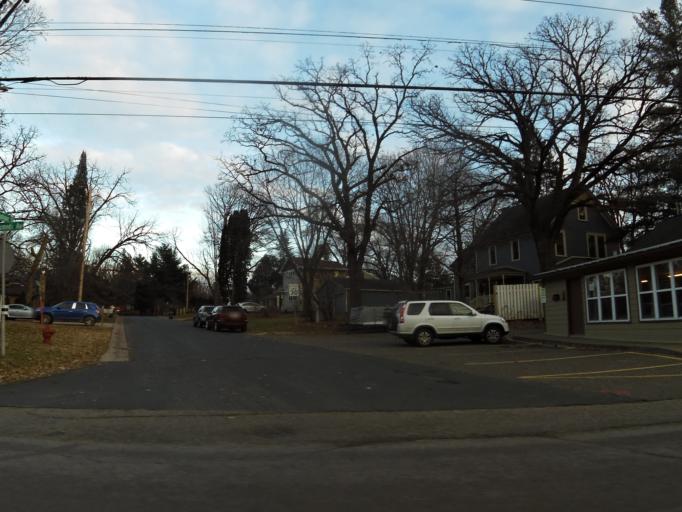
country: US
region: Minnesota
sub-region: Washington County
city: Mahtomedi
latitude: 45.0679
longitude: -92.9570
